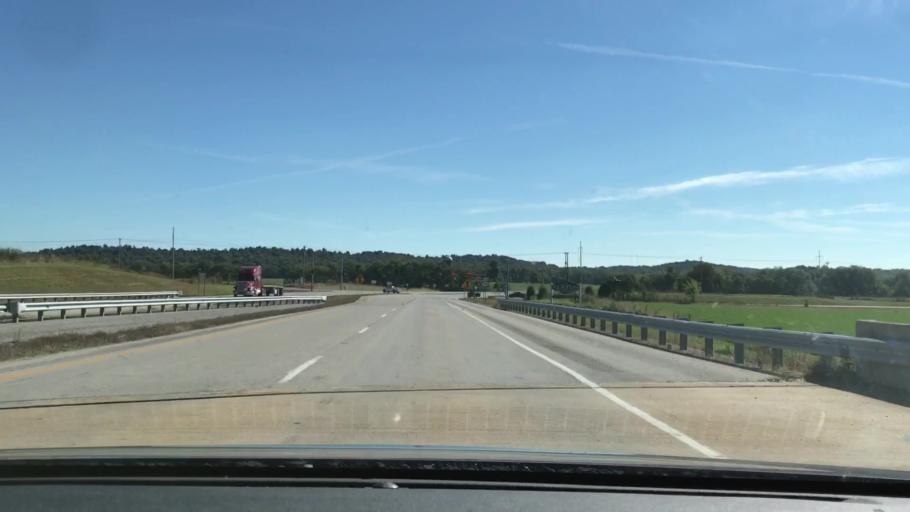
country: US
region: Kentucky
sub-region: Todd County
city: Elkton
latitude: 36.8244
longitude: -87.1539
